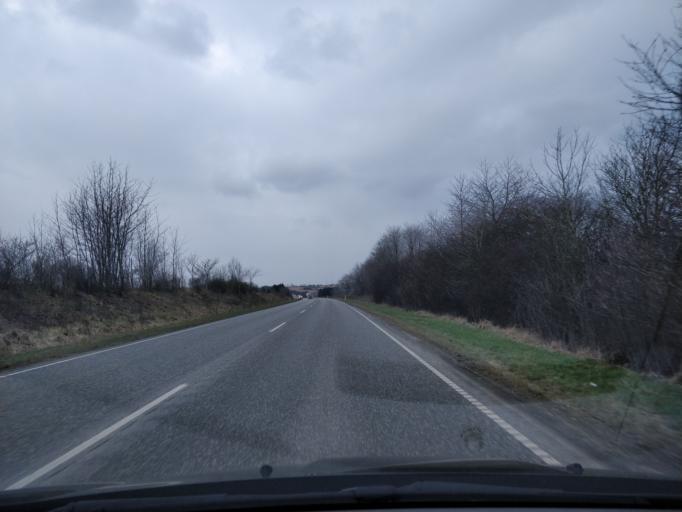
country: DK
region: South Denmark
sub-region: Vejle Kommune
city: Borkop
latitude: 55.6476
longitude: 9.6573
